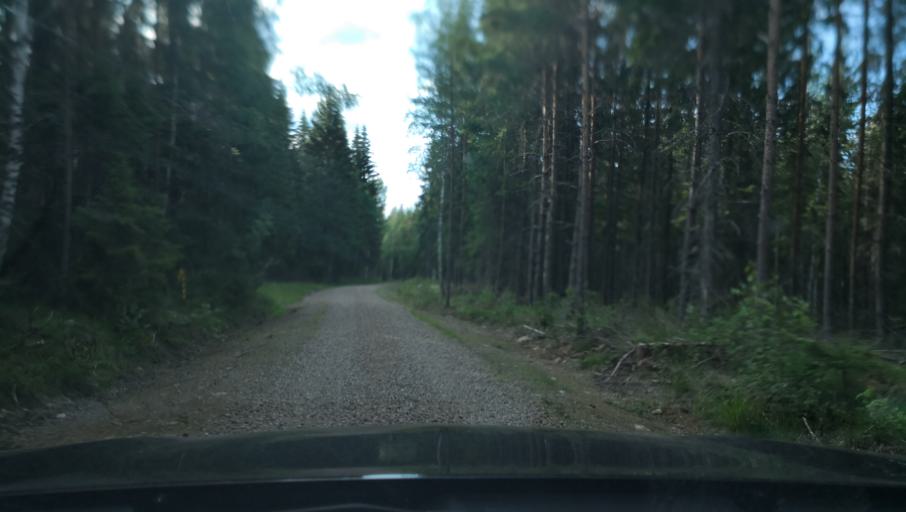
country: SE
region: Dalarna
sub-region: Ludvika Kommun
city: Ludvika
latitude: 60.0736
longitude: 15.2912
